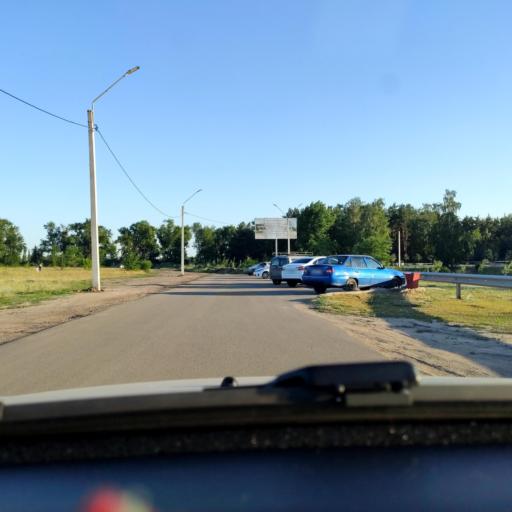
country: RU
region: Voronezj
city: Voronezh
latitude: 51.6311
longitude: 39.1578
